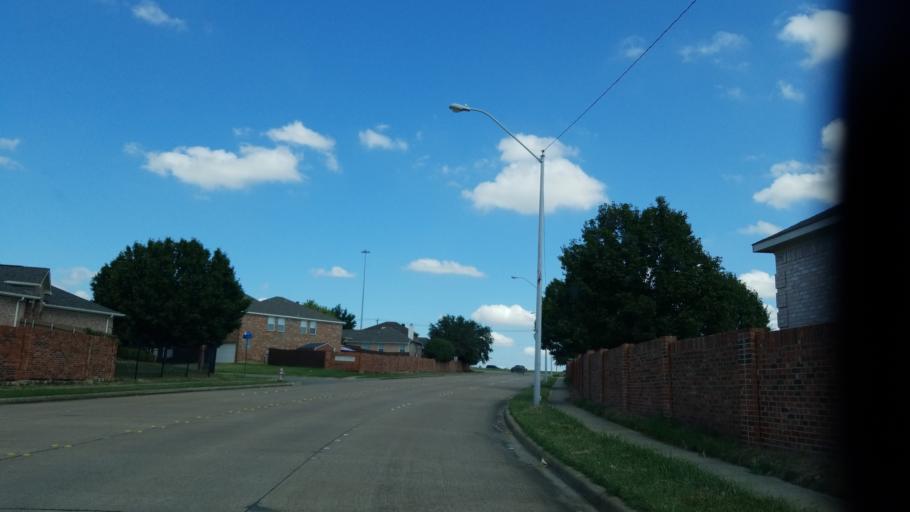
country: US
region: Texas
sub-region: Tarrant County
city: Euless
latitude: 32.8353
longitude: -97.0725
